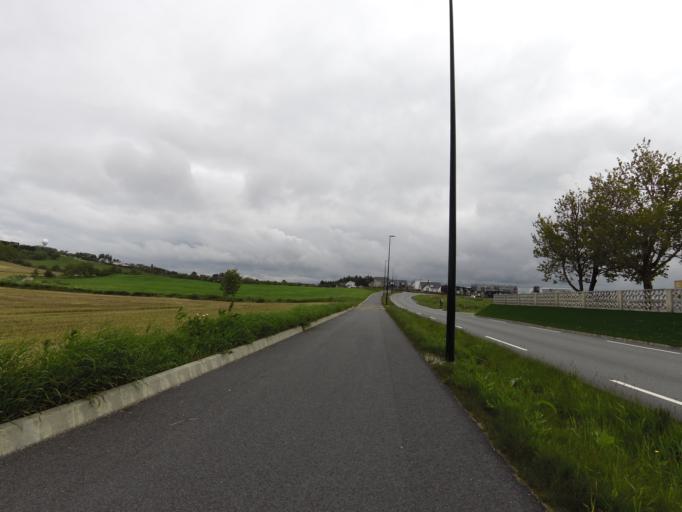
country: NO
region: Rogaland
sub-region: Sola
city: Sola
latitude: 58.8424
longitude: 5.5899
